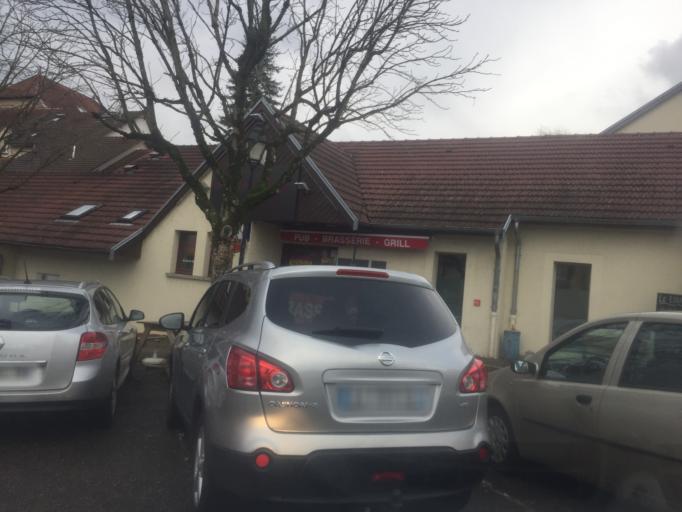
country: FR
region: Franche-Comte
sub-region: Departement du Doubs
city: Saint-Vit
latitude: 47.1825
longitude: 5.8126
